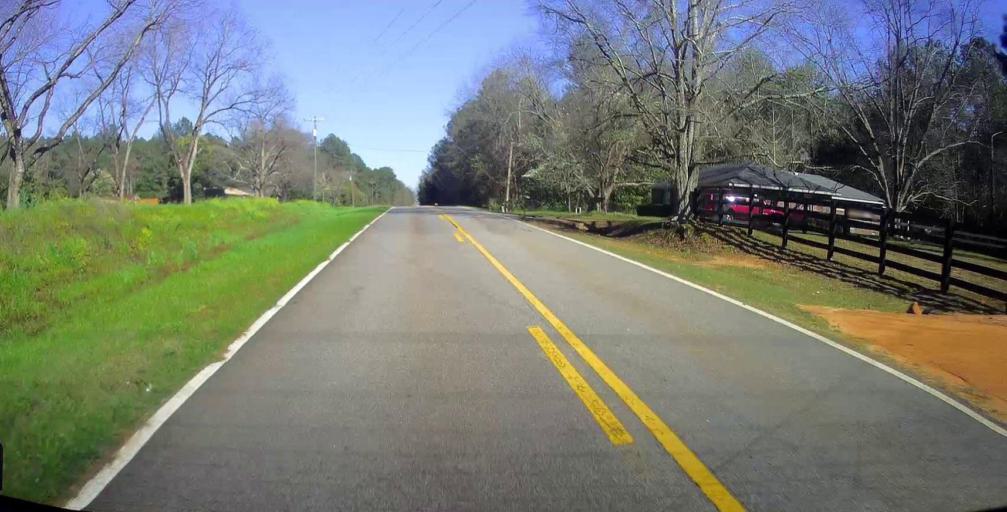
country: US
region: Georgia
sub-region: Peach County
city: Byron
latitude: 32.6442
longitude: -83.8246
